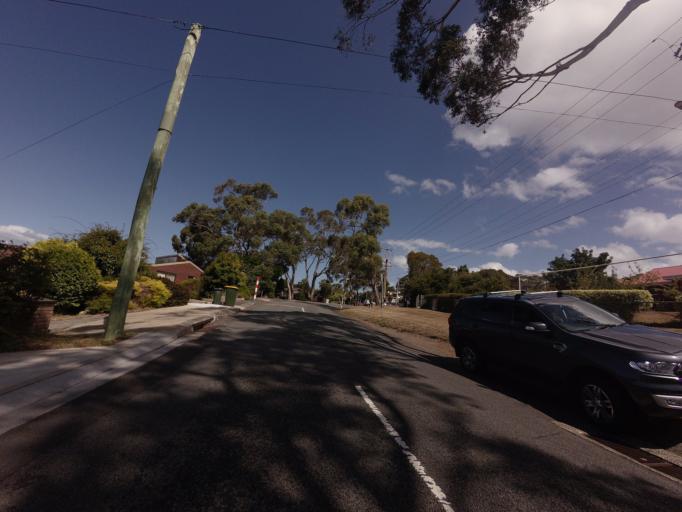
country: AU
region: Tasmania
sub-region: Hobart
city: Dynnyrne
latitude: -42.9132
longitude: 147.3236
